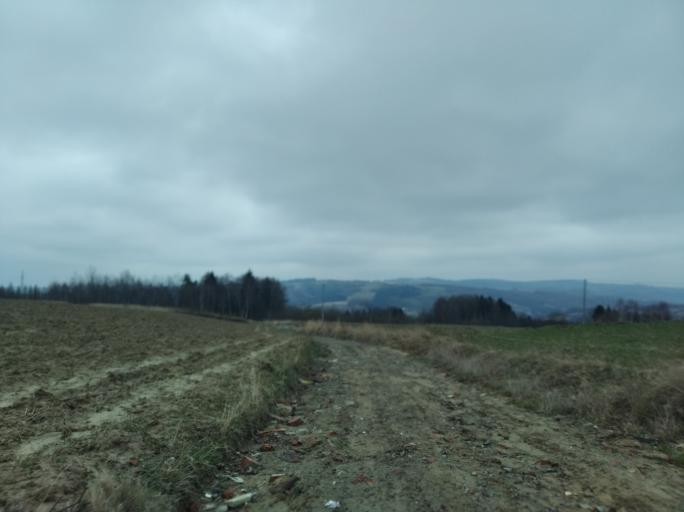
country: PL
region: Subcarpathian Voivodeship
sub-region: Powiat strzyzowski
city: Strzyzow
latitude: 49.9048
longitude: 21.8076
